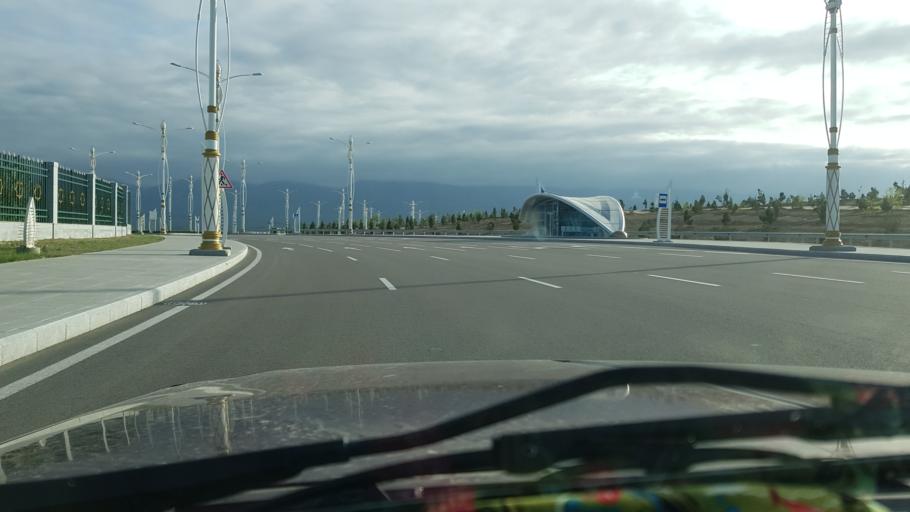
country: TM
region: Ahal
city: Ashgabat
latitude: 37.9303
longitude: 58.3320
